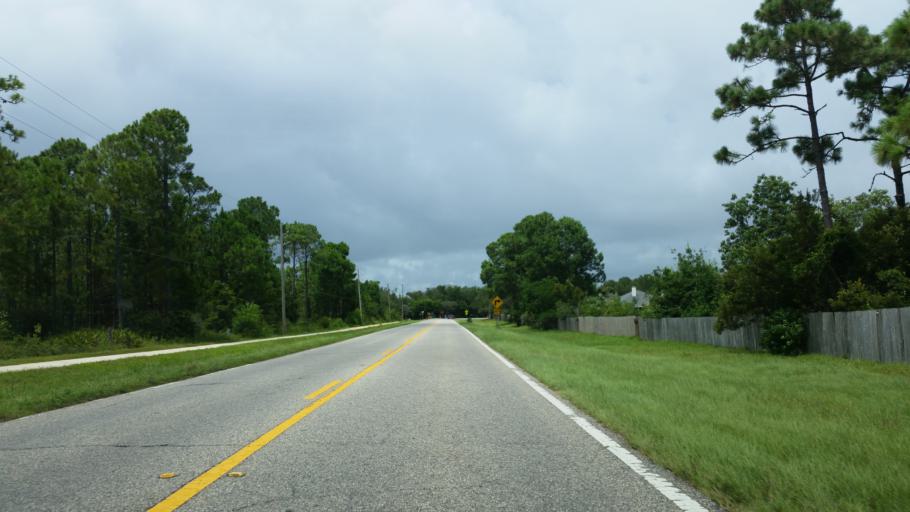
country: US
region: Florida
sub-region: Santa Rosa County
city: Woodlawn Beach
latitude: 30.4058
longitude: -86.9997
